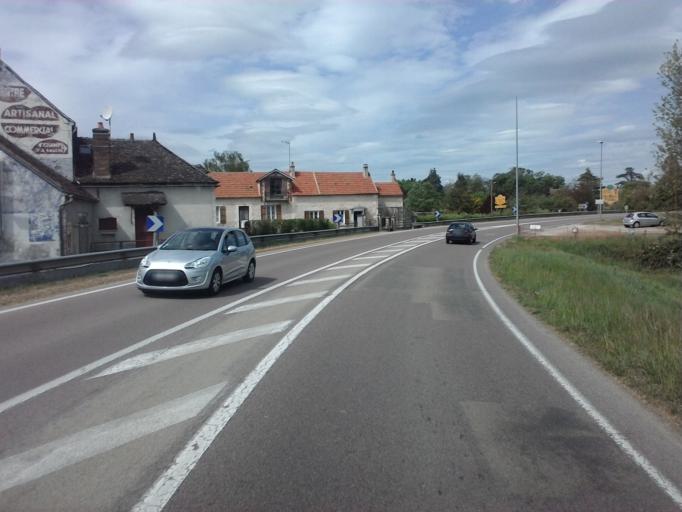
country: FR
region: Bourgogne
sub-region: Departement de l'Yonne
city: Champs-sur-Yonne
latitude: 47.7309
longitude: 3.5989
